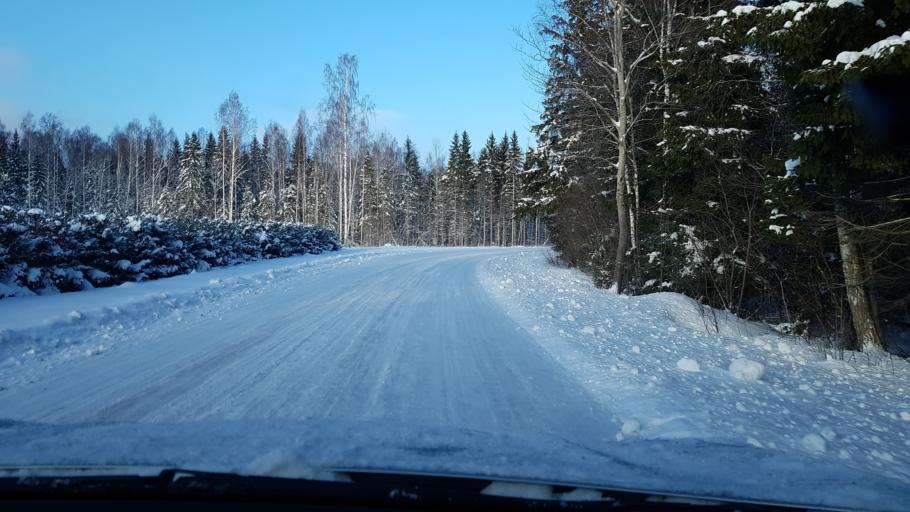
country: EE
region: Harju
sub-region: Nissi vald
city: Turba
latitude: 59.1137
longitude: 24.2217
